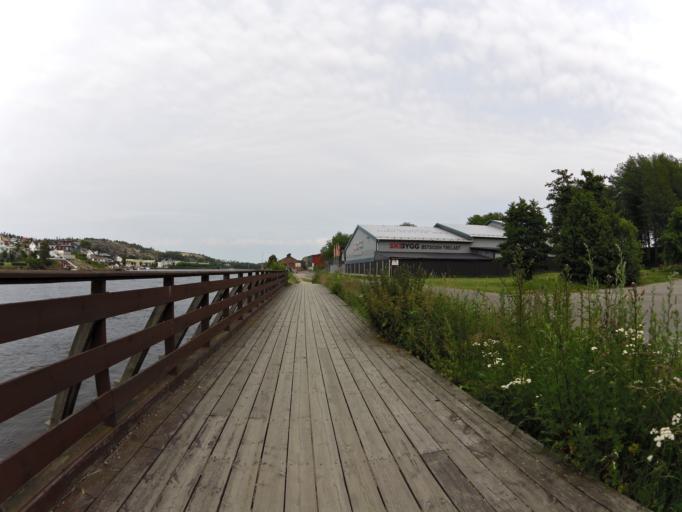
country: NO
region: Ostfold
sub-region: Fredrikstad
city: Fredrikstad
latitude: 59.2112
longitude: 10.9629
